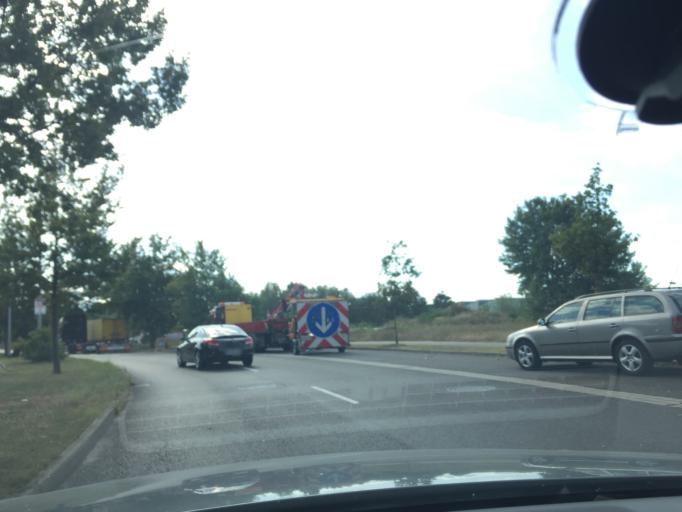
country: DE
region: Brandenburg
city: Grunheide
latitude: 52.3882
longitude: 13.7991
